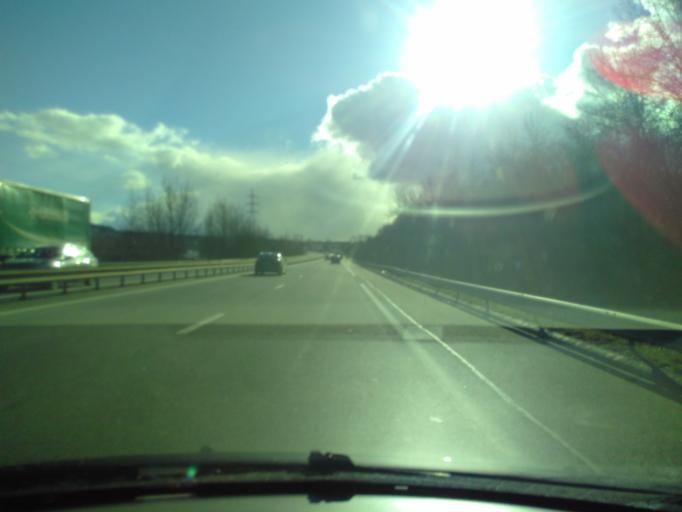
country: FR
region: Rhone-Alpes
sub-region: Departement de la Haute-Savoie
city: Meythet
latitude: 45.9179
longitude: 6.1008
